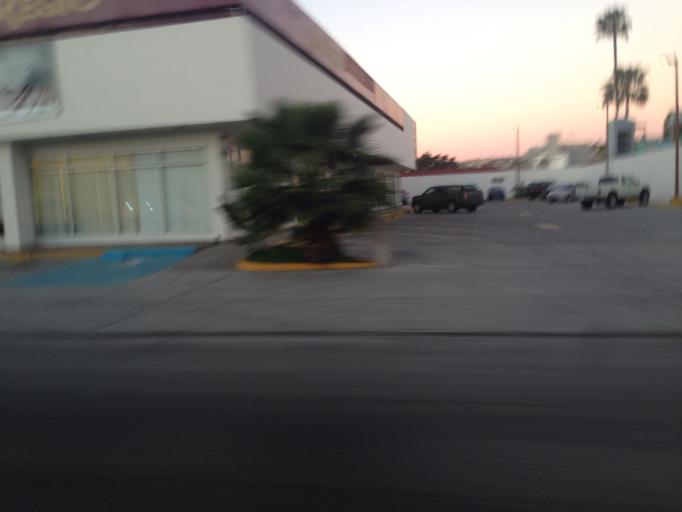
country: MX
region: Baja California
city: Tijuana
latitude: 32.5161
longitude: -117.0114
